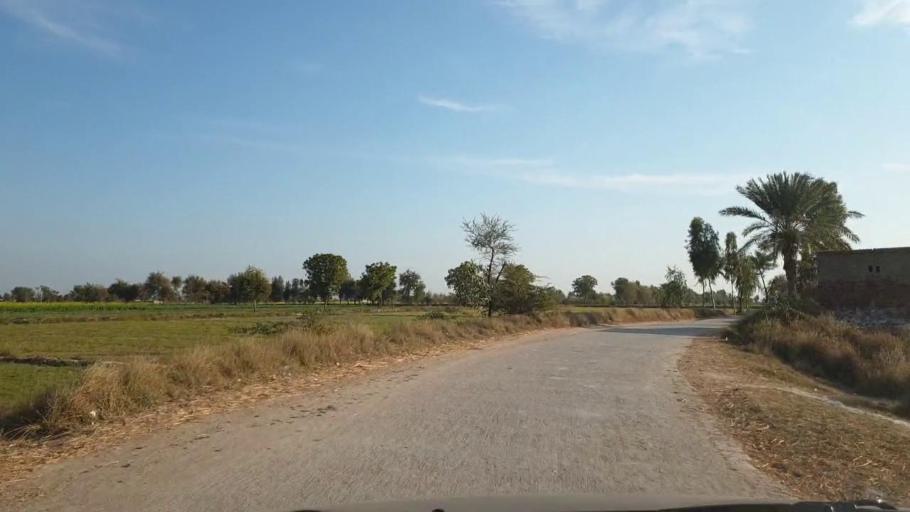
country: PK
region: Sindh
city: Khadro
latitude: 26.1892
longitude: 68.7497
